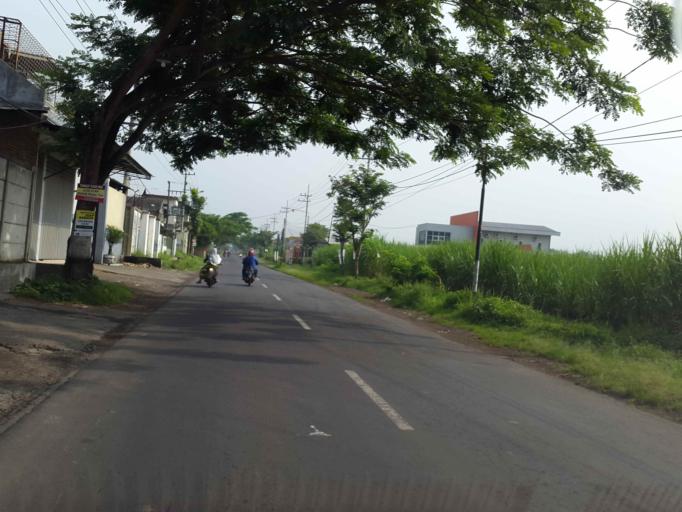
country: ID
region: East Java
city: Tamiajeng
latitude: -7.9602
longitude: 112.6976
